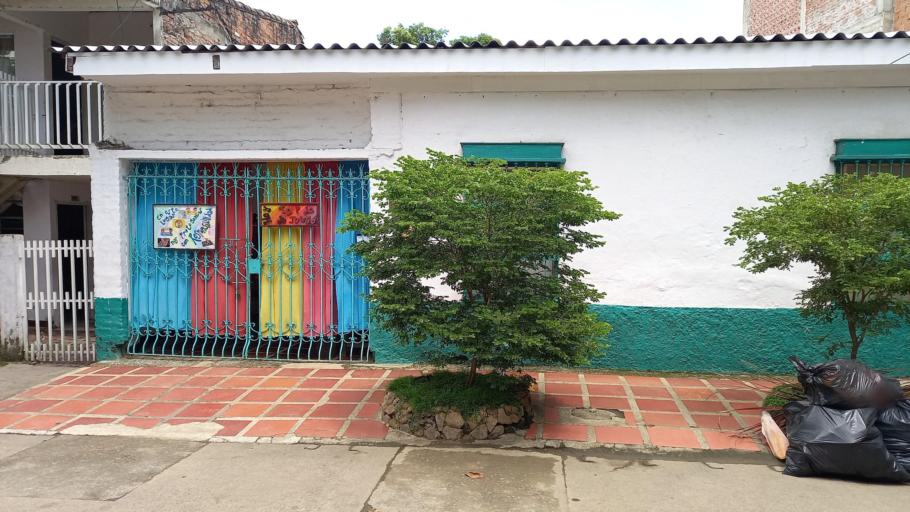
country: CO
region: Valle del Cauca
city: Jamundi
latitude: 3.2603
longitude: -76.5435
